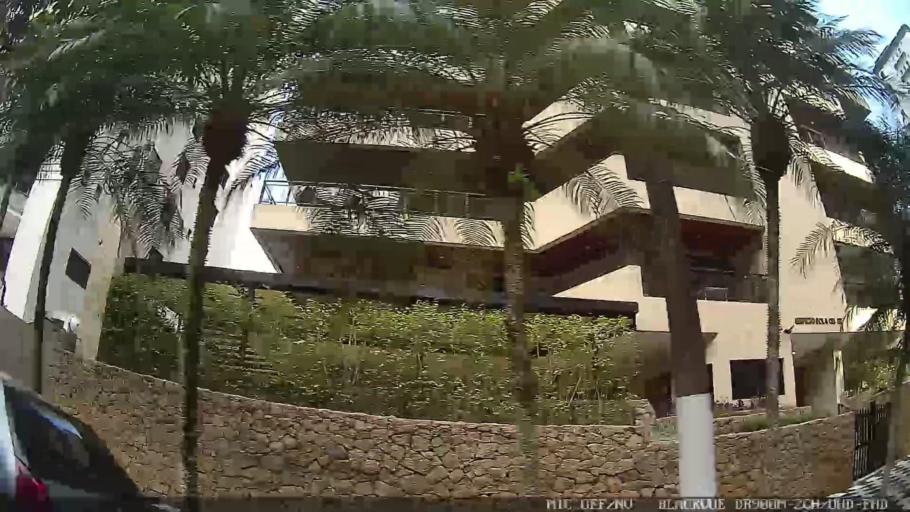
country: BR
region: Sao Paulo
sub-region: Guaruja
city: Guaruja
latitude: -23.9965
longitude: -46.2647
